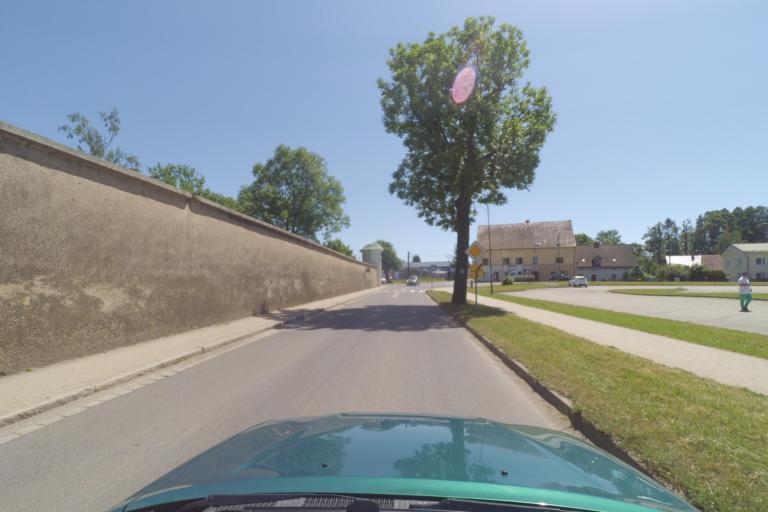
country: PL
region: Lower Silesian Voivodeship
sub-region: Powiat kamiennogorski
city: Krzeszow
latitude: 50.7309
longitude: 16.0682
